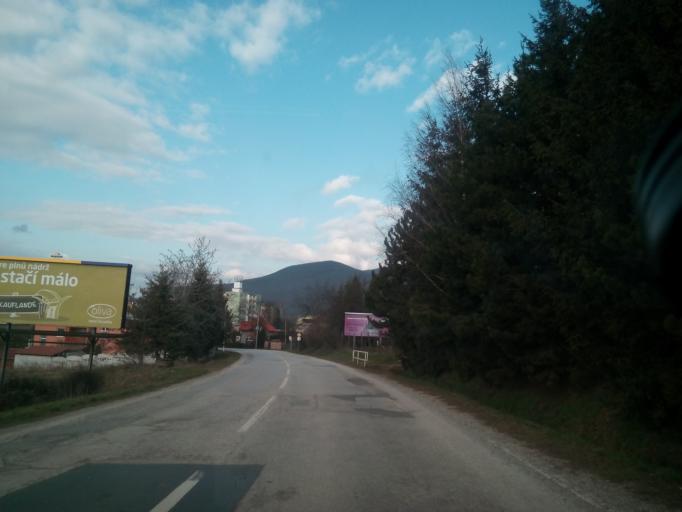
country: SK
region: Kosicky
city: Roznava
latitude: 48.6586
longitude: 20.5454
